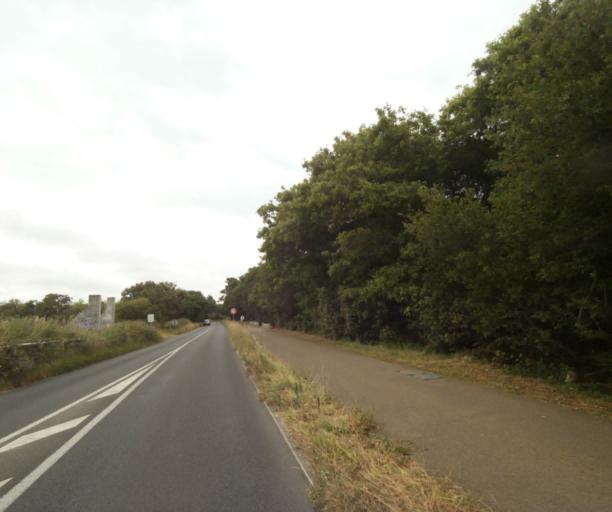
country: FR
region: Pays de la Loire
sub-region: Departement de la Vendee
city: Chateau-d'Olonne
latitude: 46.4635
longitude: -1.7231
